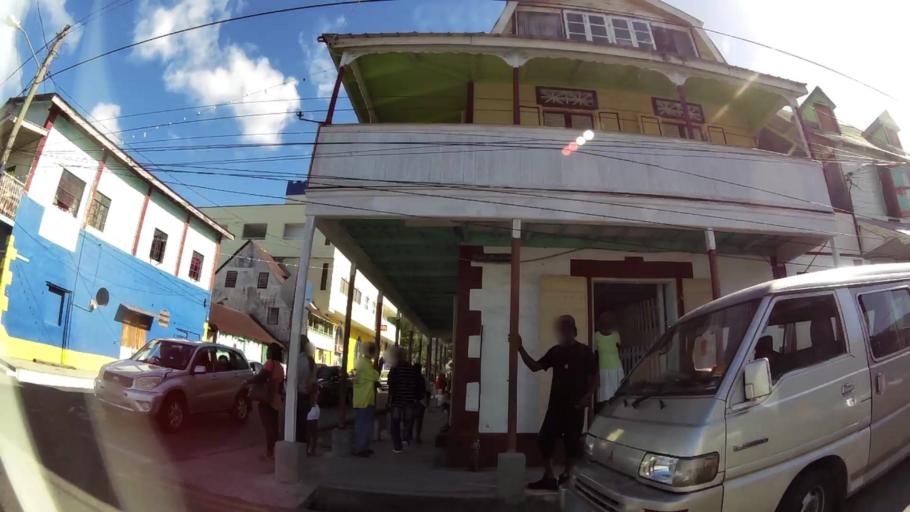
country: LC
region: Soufriere
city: Soufriere
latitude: 13.8537
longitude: -61.0593
